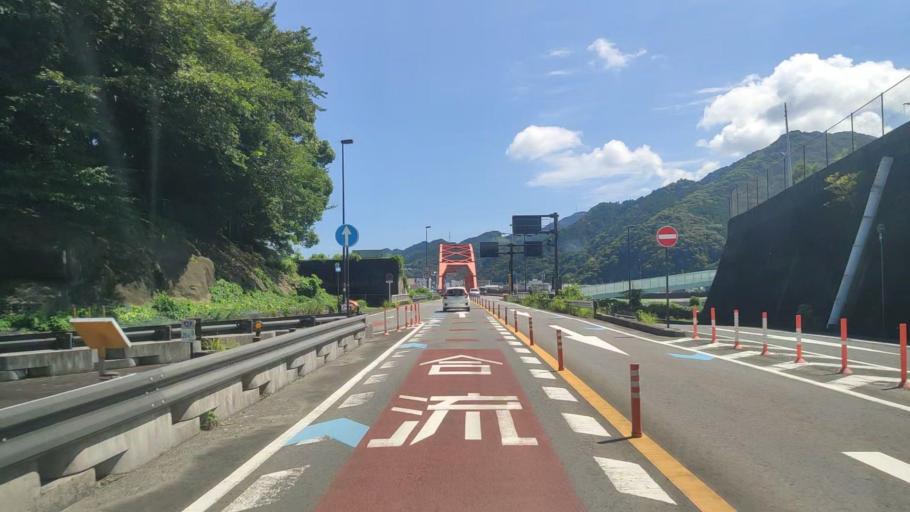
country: JP
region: Wakayama
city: Shingu
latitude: 33.7357
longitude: 135.9883
